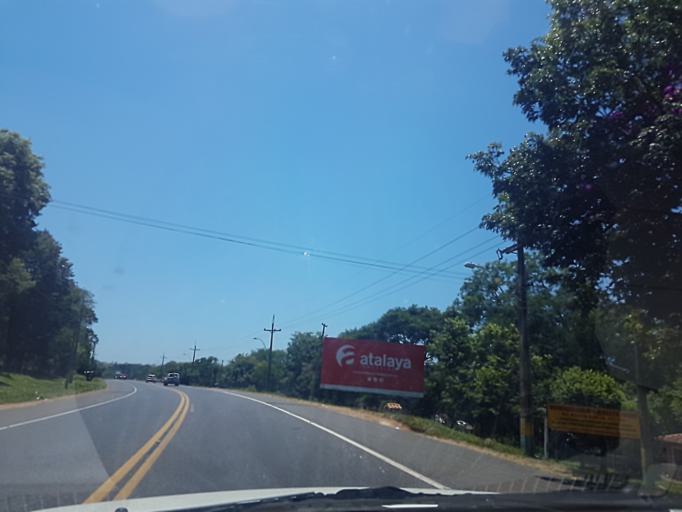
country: PY
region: Cordillera
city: Caacupe
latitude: -25.3910
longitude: -57.0754
